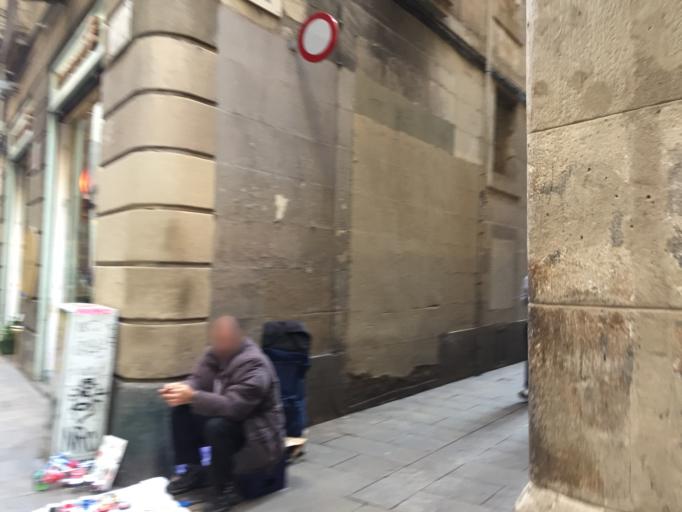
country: ES
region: Catalonia
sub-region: Provincia de Barcelona
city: Ciutat Vella
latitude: 41.3813
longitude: 2.1742
